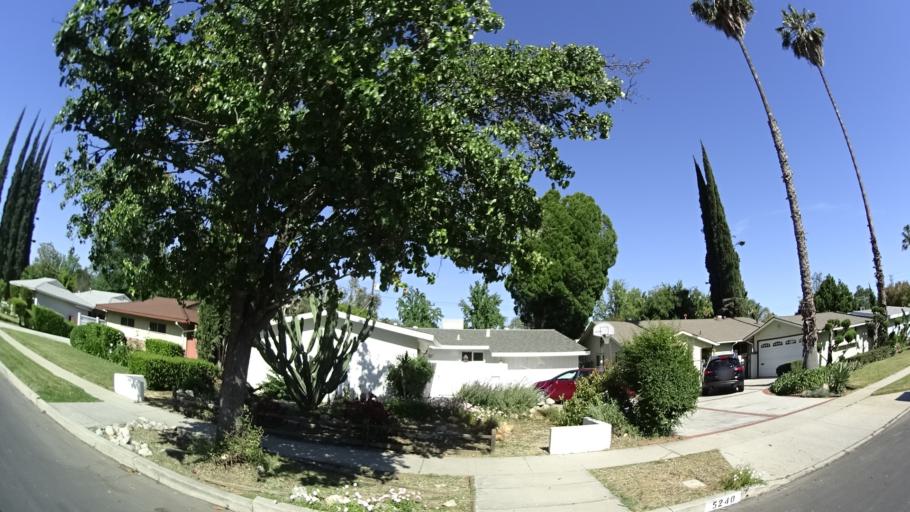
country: US
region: California
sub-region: Los Angeles County
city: Sherman Oaks
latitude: 34.1661
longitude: -118.4282
